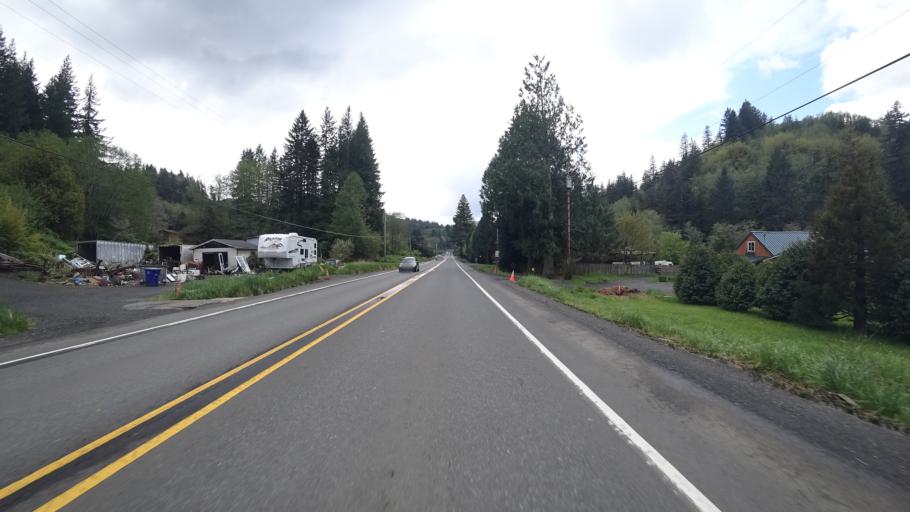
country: US
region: Oregon
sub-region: Lincoln County
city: Rose Lodge
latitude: 45.0169
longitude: -123.8712
